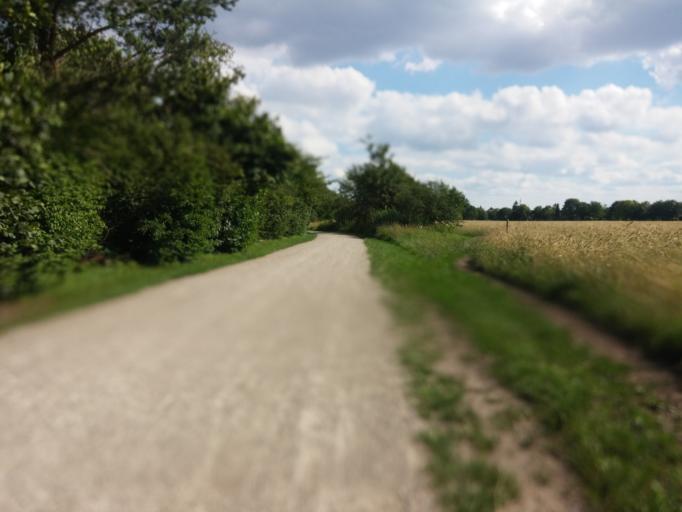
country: DE
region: Bavaria
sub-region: Upper Bavaria
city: Unterfoehring
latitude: 48.1504
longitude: 11.6638
